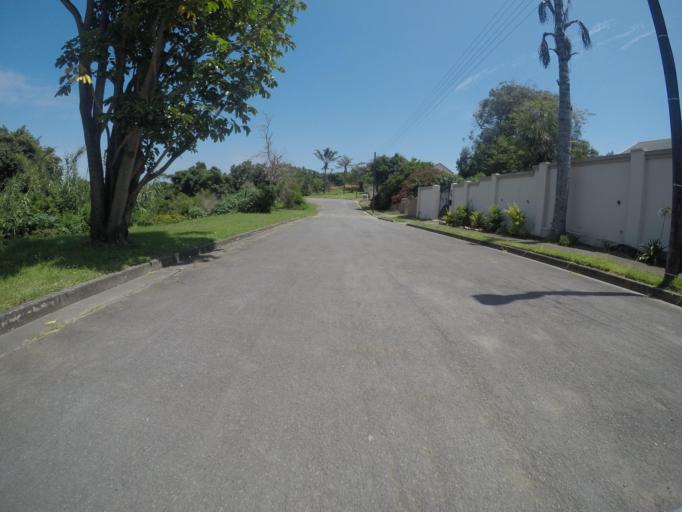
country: ZA
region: Eastern Cape
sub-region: Buffalo City Metropolitan Municipality
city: East London
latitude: -33.0030
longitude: 27.9180
